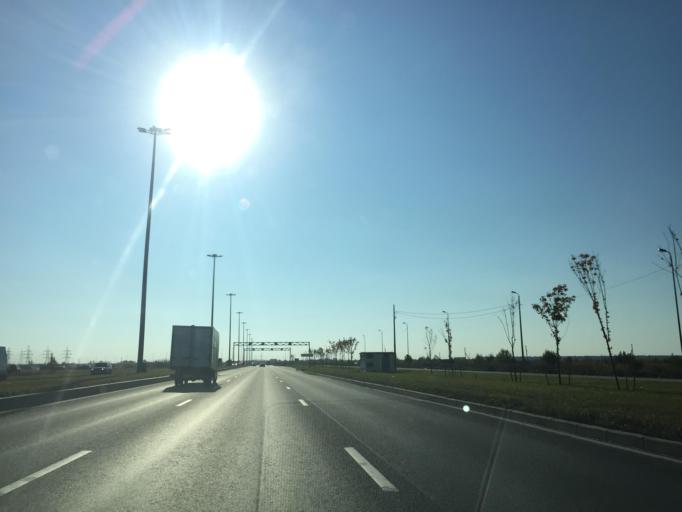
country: RU
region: St.-Petersburg
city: Petro-Slavyanka
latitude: 59.7739
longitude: 30.4992
